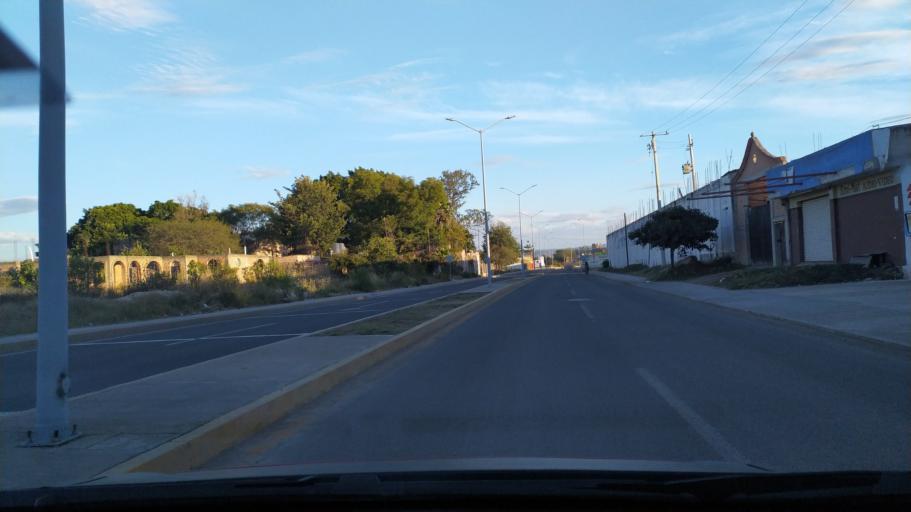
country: MX
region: Guanajuato
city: Ciudad Manuel Doblado
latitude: 20.7345
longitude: -101.9482
